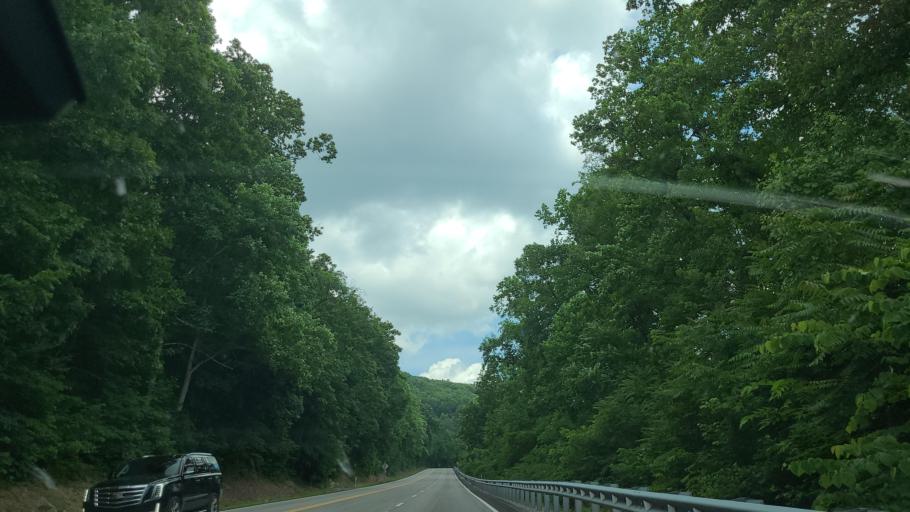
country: US
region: Tennessee
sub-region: Cumberland County
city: Lake Tansi
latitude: 35.7628
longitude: -85.0506
